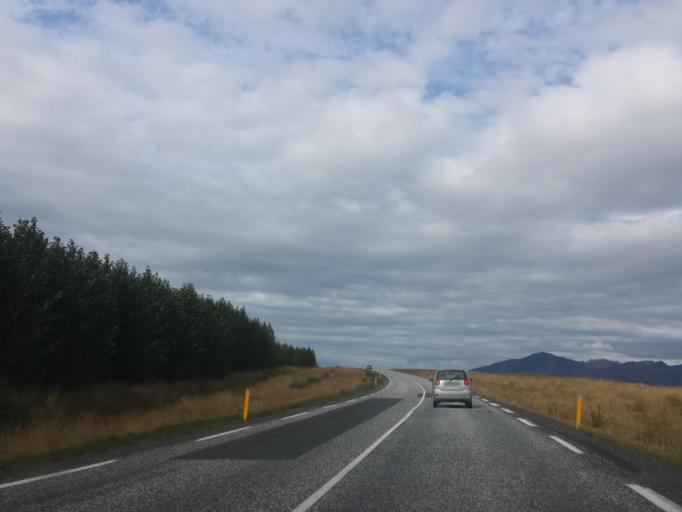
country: IS
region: West
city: Borgarnes
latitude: 64.3583
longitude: -21.8075
